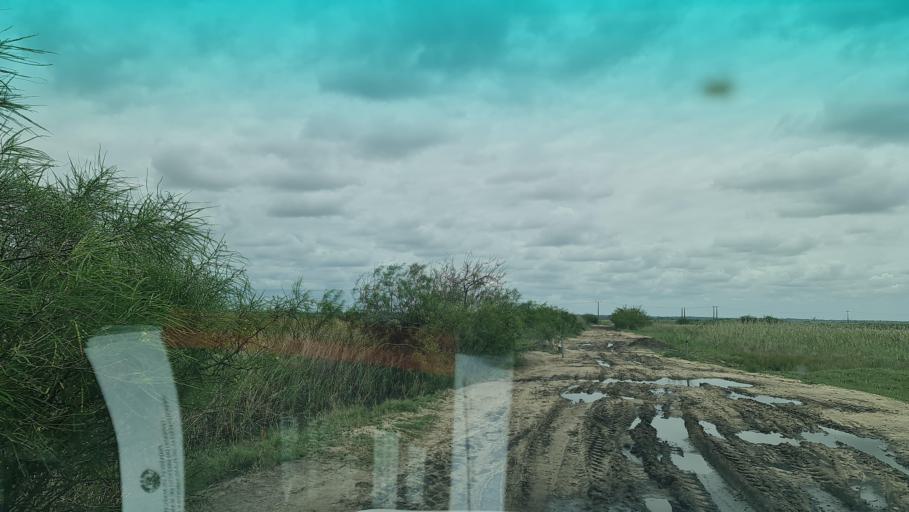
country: MZ
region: Maputo City
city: Maputo
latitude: -25.7255
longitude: 32.7010
